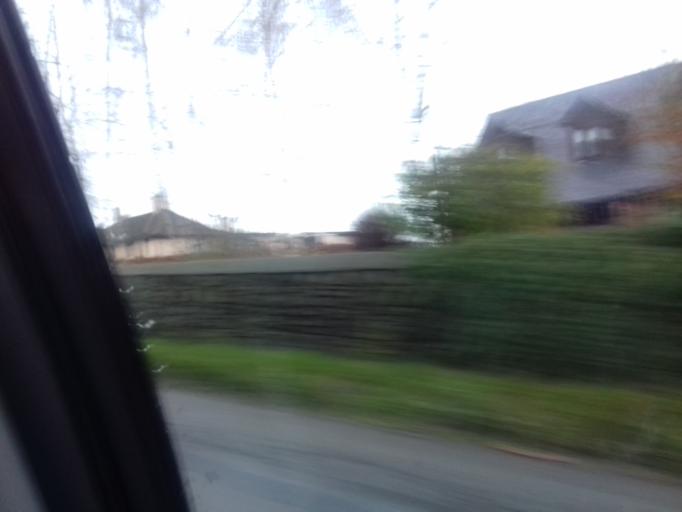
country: IE
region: Leinster
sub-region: County Carlow
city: Bagenalstown
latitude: 52.6573
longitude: -6.9906
